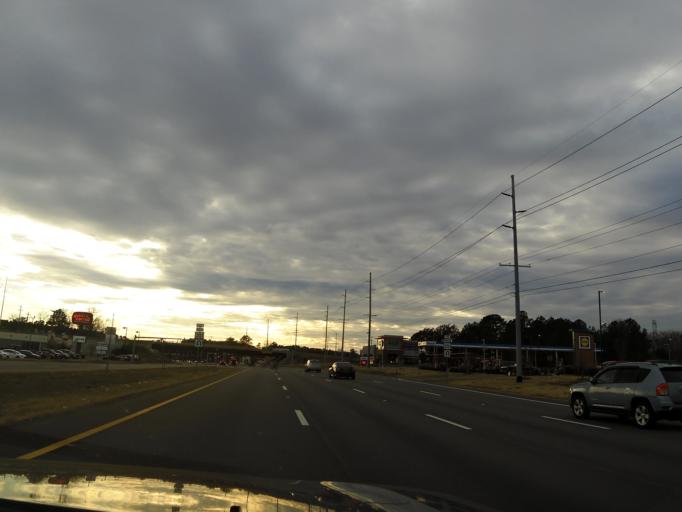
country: US
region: North Carolina
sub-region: Nash County
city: Rocky Mount
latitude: 35.9695
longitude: -77.8122
